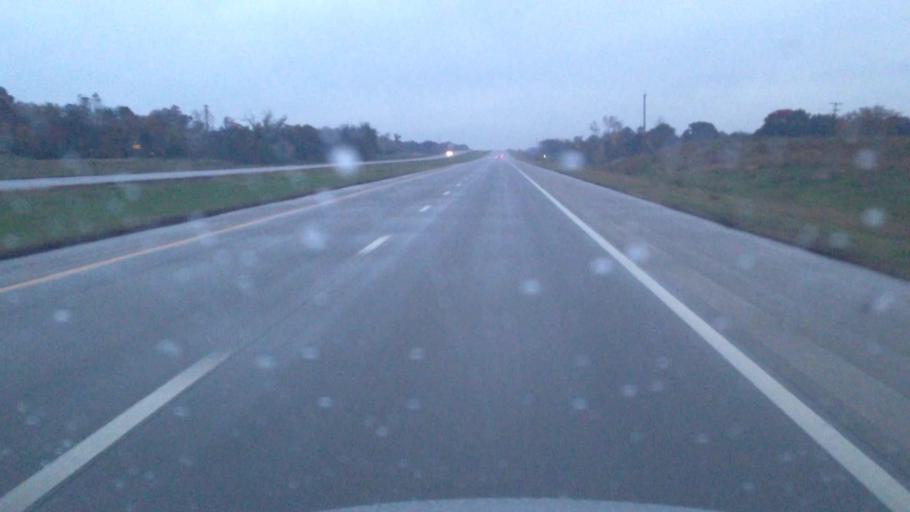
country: US
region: Kansas
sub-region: Douglas County
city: Baldwin City
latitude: 38.7694
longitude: -95.2687
